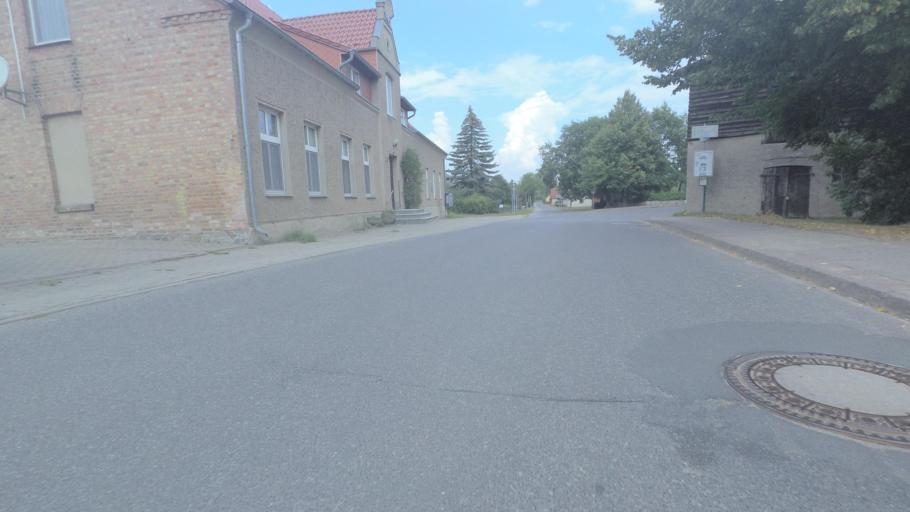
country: DE
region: Mecklenburg-Vorpommern
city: Borrentin
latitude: 53.8108
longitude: 12.9148
